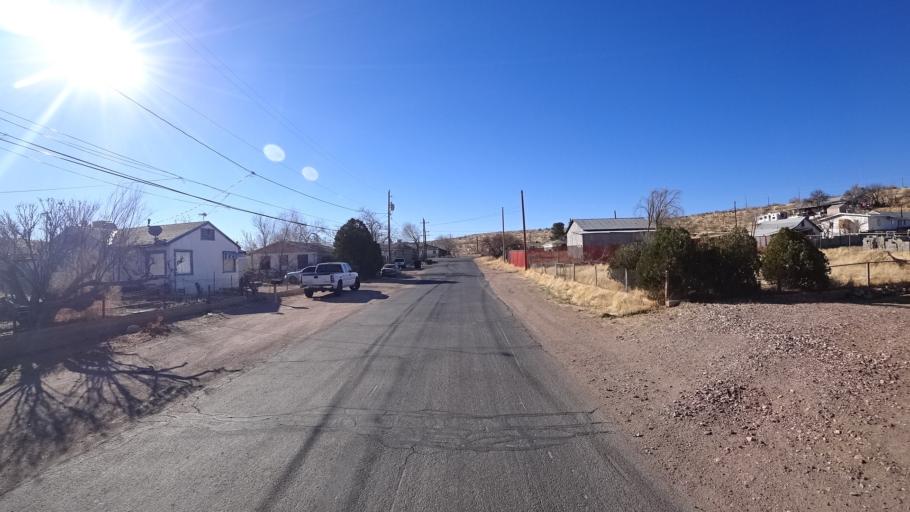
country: US
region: Arizona
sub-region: Mohave County
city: Kingman
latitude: 35.1842
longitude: -114.0501
